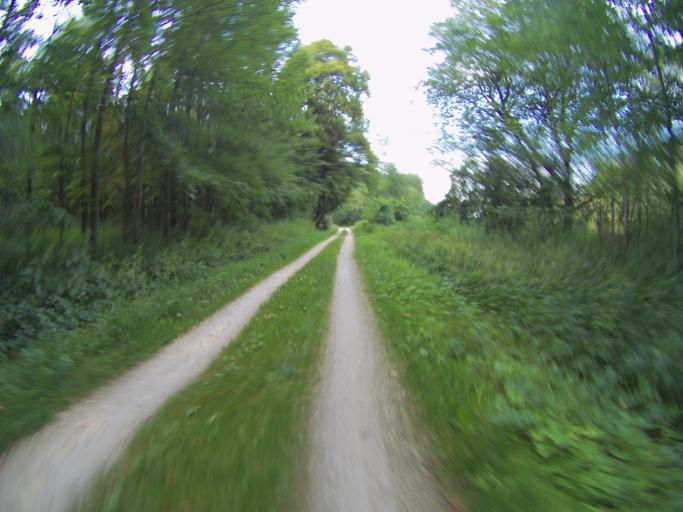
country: DE
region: Bavaria
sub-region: Upper Bavaria
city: Freising
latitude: 48.3768
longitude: 11.7349
